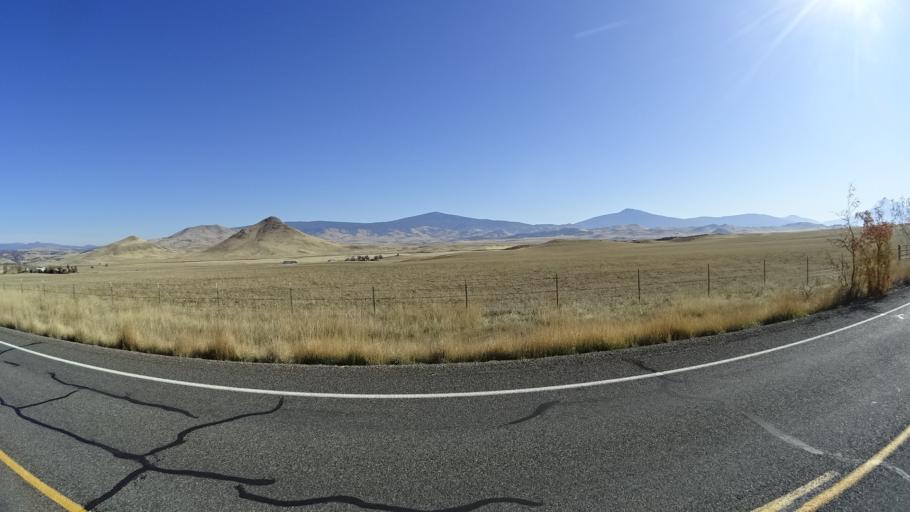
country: US
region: California
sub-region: Siskiyou County
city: Montague
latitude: 41.8121
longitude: -122.4984
